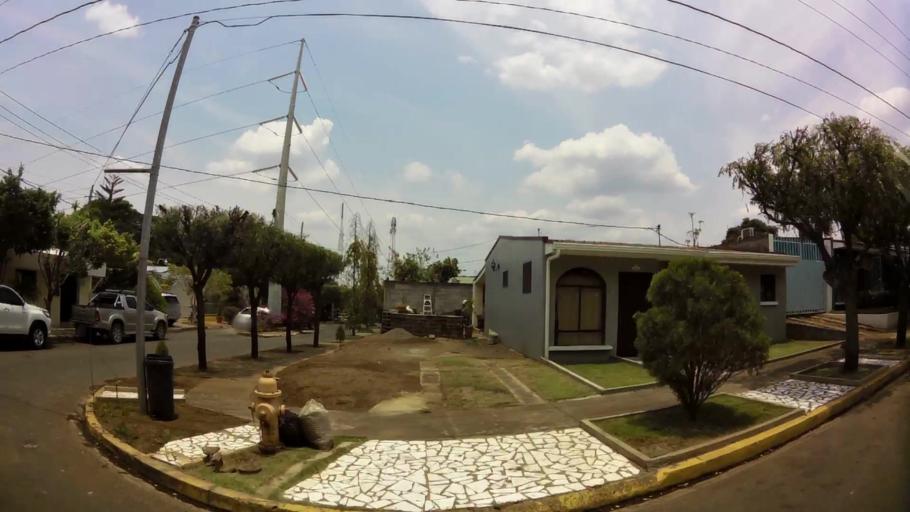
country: NI
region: Managua
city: Managua
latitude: 12.1212
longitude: -86.2857
